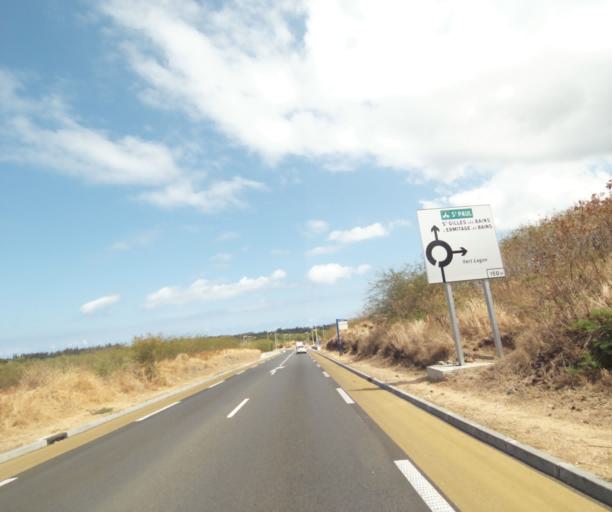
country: RE
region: Reunion
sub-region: Reunion
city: Trois-Bassins
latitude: -21.0890
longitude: 55.2391
